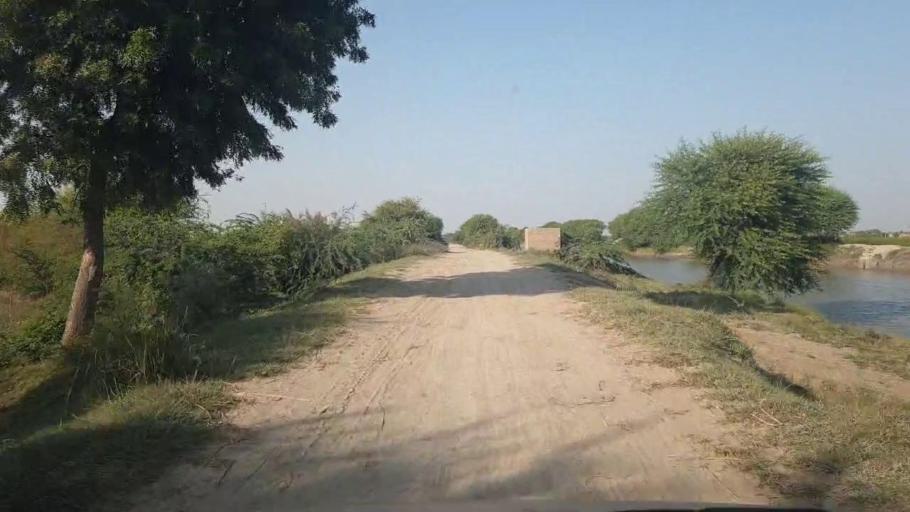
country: PK
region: Sindh
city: Badin
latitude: 24.6451
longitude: 68.8151
